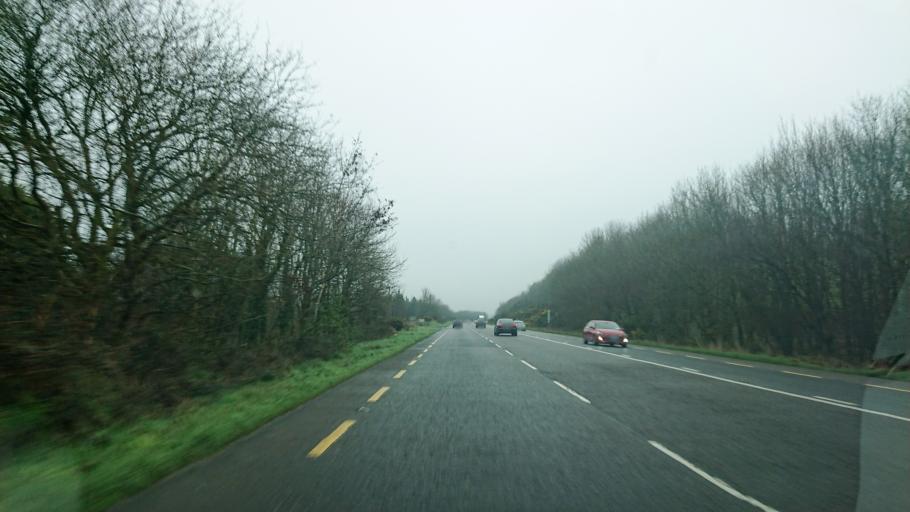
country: IE
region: Munster
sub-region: County Cork
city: Cork
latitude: 51.8199
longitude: -8.5338
